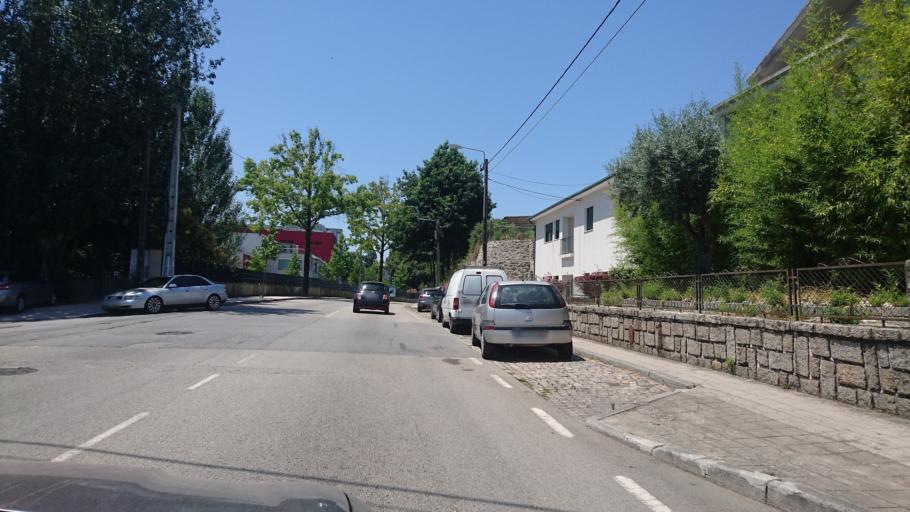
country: PT
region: Porto
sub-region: Gondomar
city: Baguim do Monte
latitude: 41.2045
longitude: -8.5537
